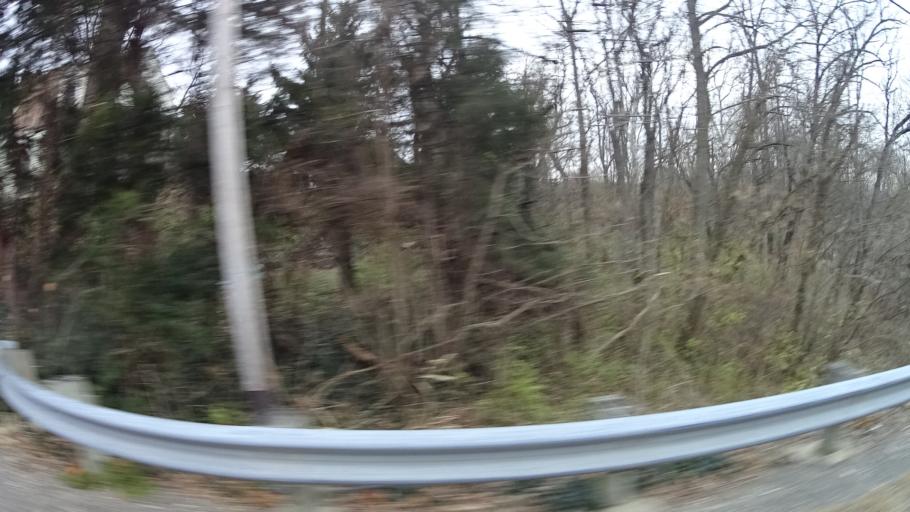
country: US
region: Ohio
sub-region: Lorain County
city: Lagrange
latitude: 41.2343
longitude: -82.0816
